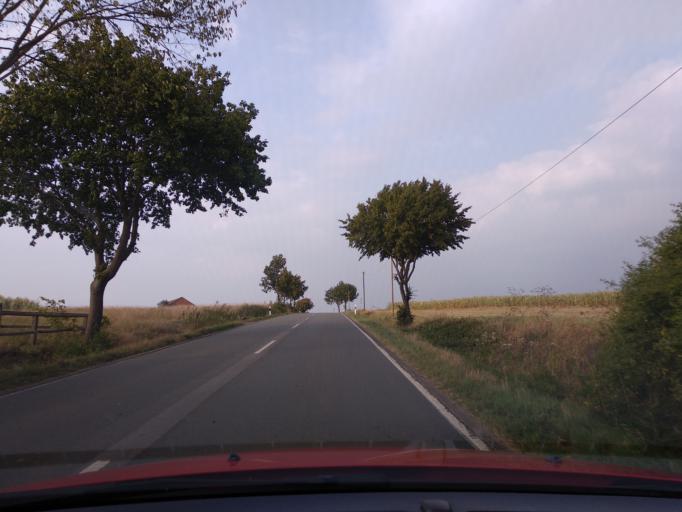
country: DE
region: Hesse
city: Liebenau
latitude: 51.5436
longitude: 9.2916
